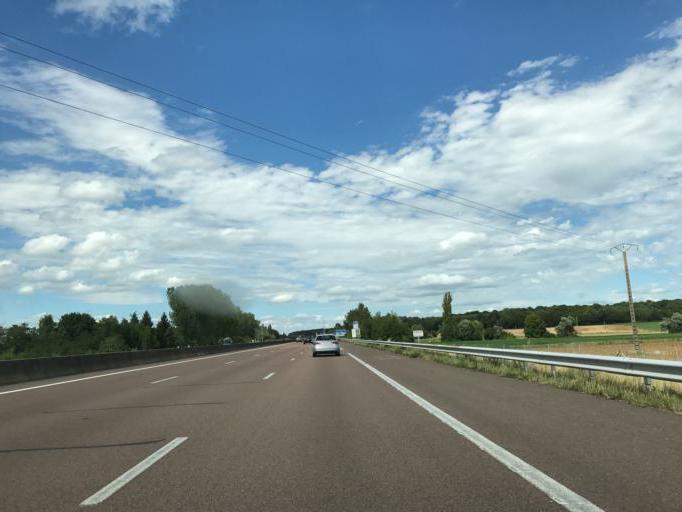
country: FR
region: Bourgogne
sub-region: Departement de Saone-et-Loire
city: Demigny
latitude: 46.9512
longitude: 4.8317
